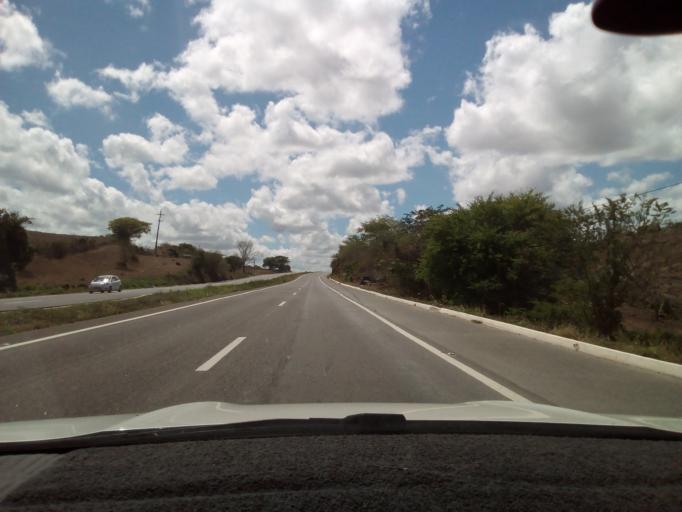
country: BR
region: Paraiba
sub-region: Massaranduba
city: Massaranduba
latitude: -7.2565
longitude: -35.8184
